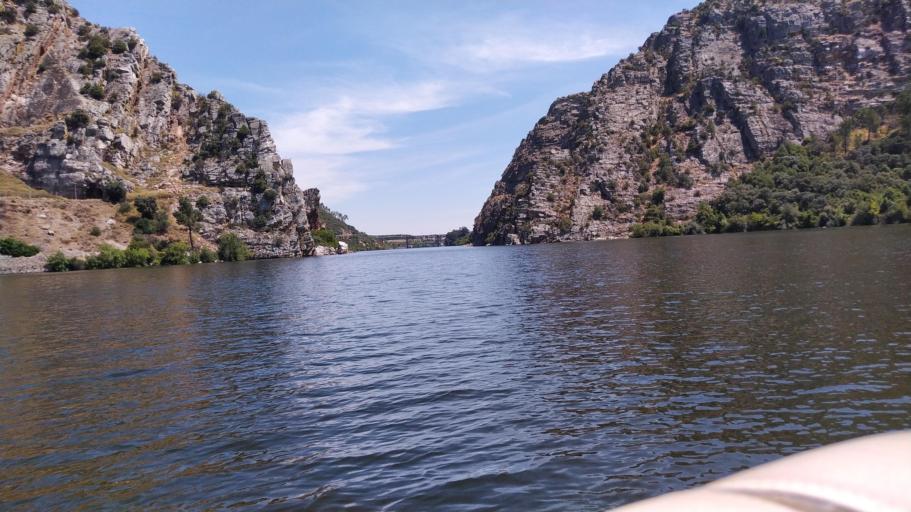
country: PT
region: Portalegre
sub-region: Nisa
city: Nisa
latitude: 39.6417
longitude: -7.6913
